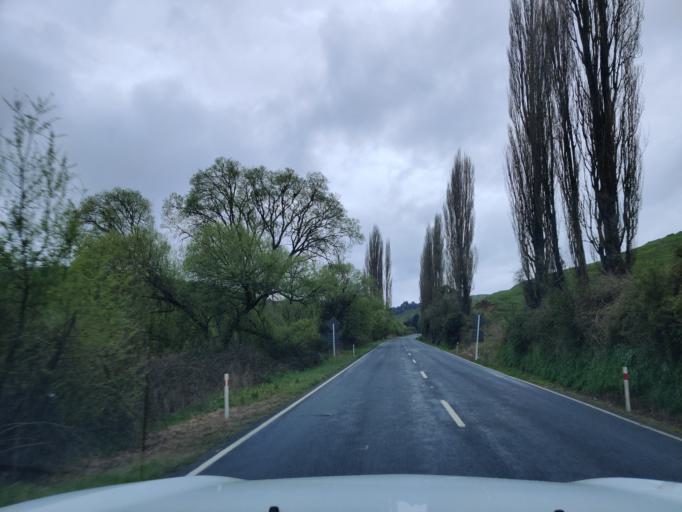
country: NZ
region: Waikato
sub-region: Otorohanga District
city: Otorohanga
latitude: -38.5626
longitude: 175.1977
